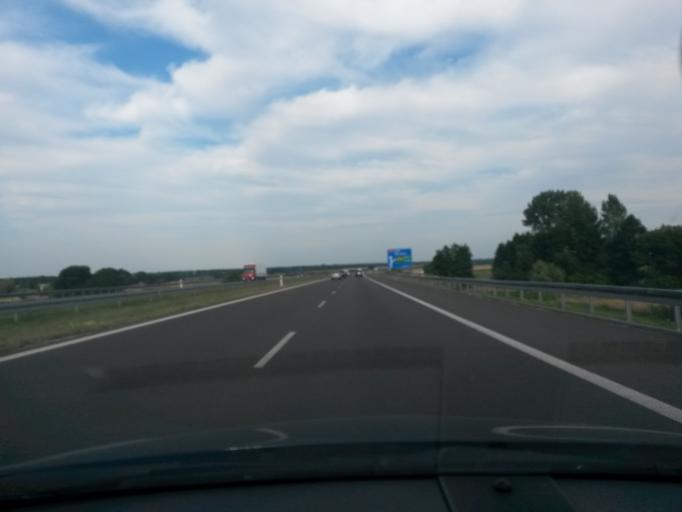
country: PL
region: Greater Poland Voivodeship
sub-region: Powiat kolski
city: Koscielec
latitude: 52.1420
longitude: 18.5774
